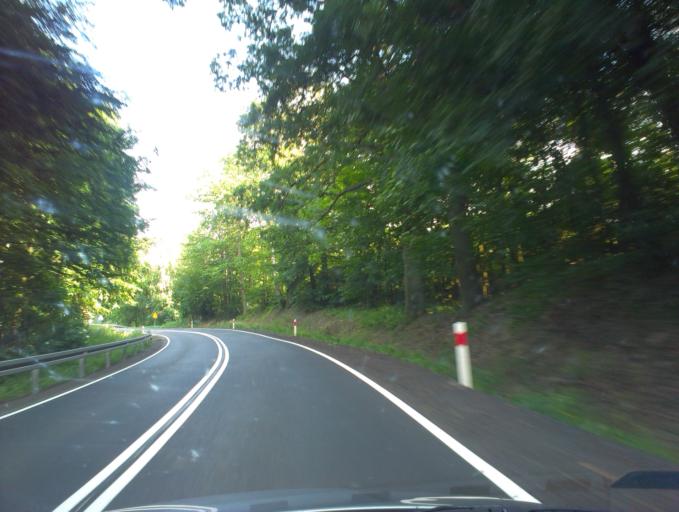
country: PL
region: West Pomeranian Voivodeship
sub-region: Powiat szczecinecki
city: Borne Sulinowo
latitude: 53.6228
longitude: 16.5165
